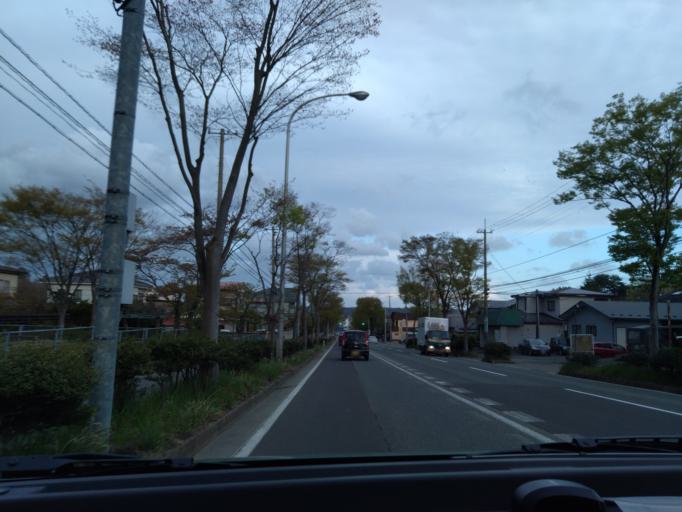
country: JP
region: Akita
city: Akita
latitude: 39.7328
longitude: 140.1420
